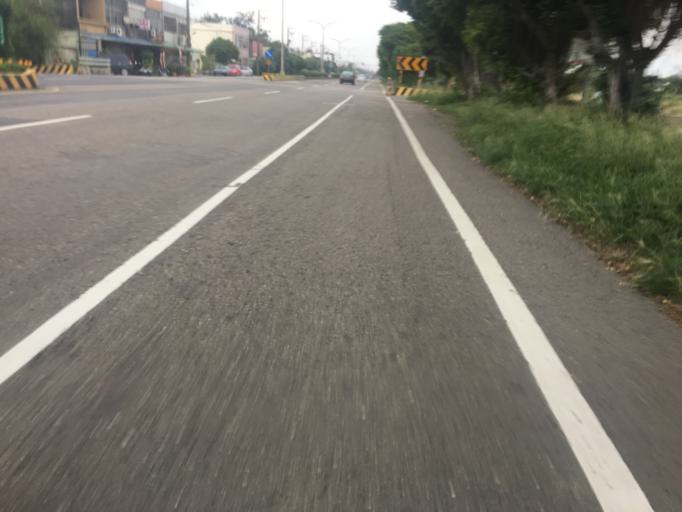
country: TW
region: Taiwan
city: Taoyuan City
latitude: 25.0866
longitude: 121.2241
